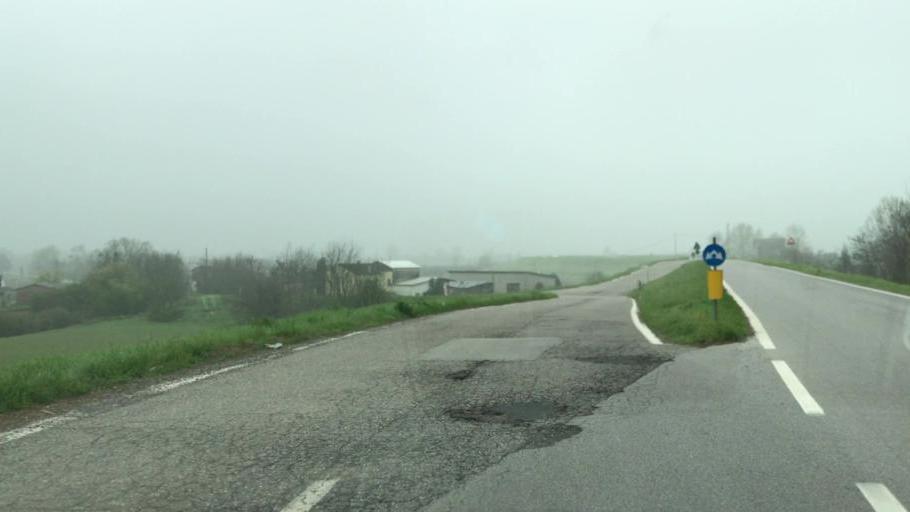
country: IT
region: Lombardy
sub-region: Provincia di Mantova
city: San Benedetto Po
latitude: 45.0360
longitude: 10.9212
